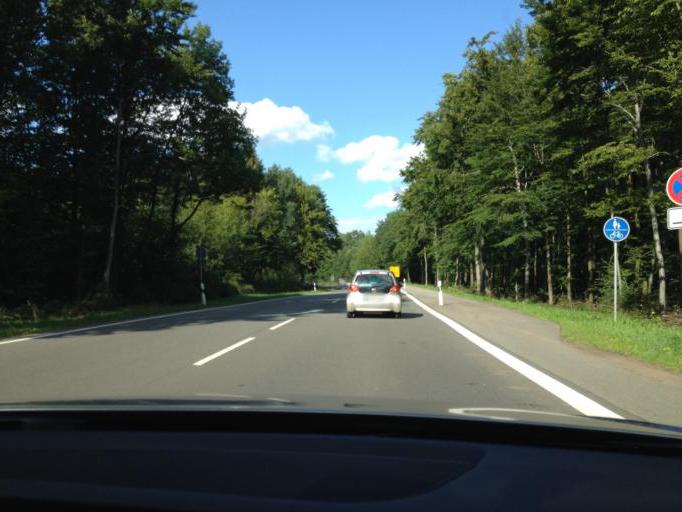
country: DE
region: Saarland
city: Lebach
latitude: 49.4255
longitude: 6.8911
